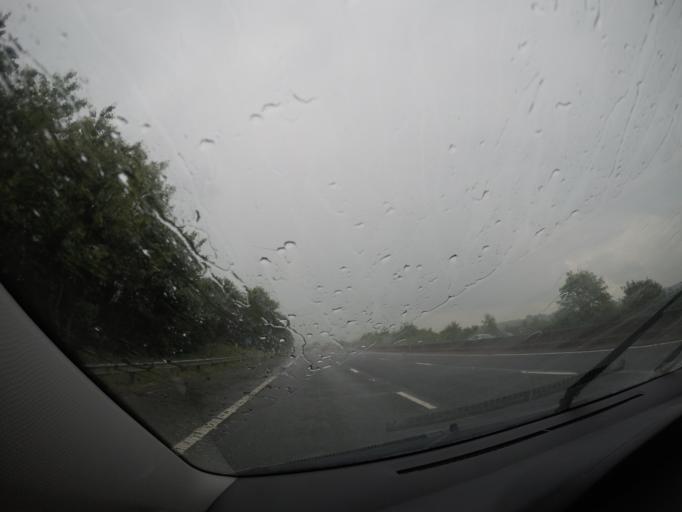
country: GB
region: England
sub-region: Cumbria
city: Penrith
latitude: 54.6667
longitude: -2.7737
